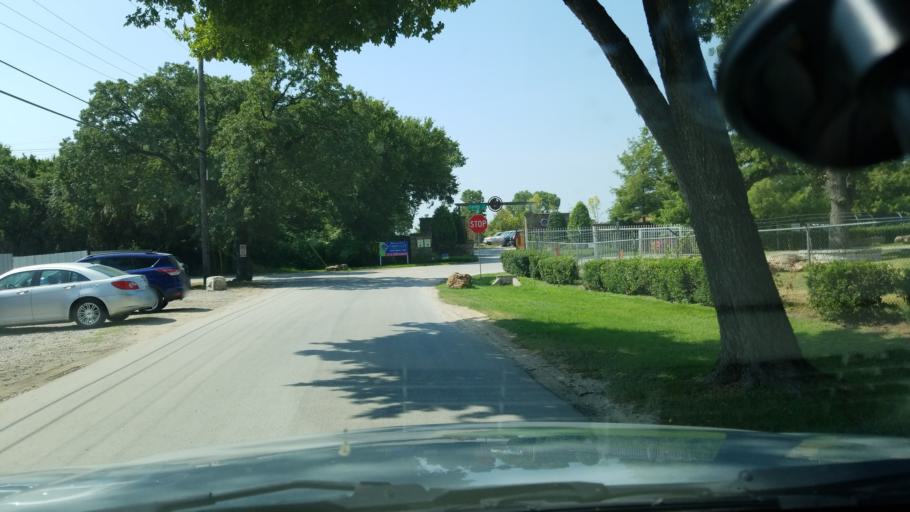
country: US
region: Texas
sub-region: Dallas County
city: Irving
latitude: 32.8609
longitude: -96.9059
